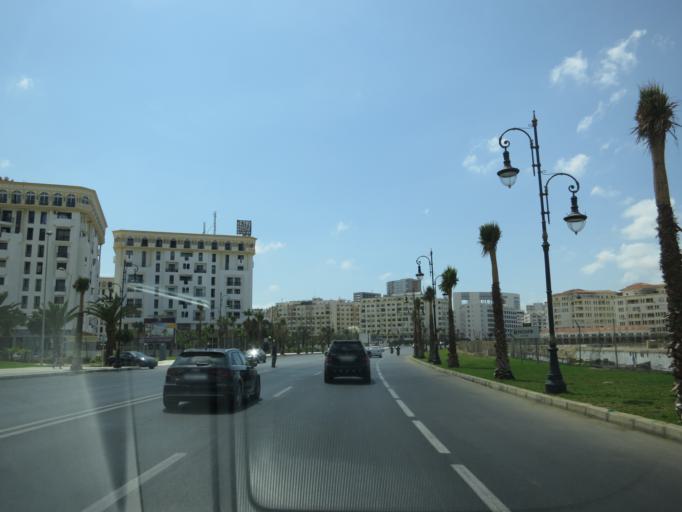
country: MA
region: Tanger-Tetouan
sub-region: Tanger-Assilah
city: Tangier
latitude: 35.7760
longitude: -5.7790
